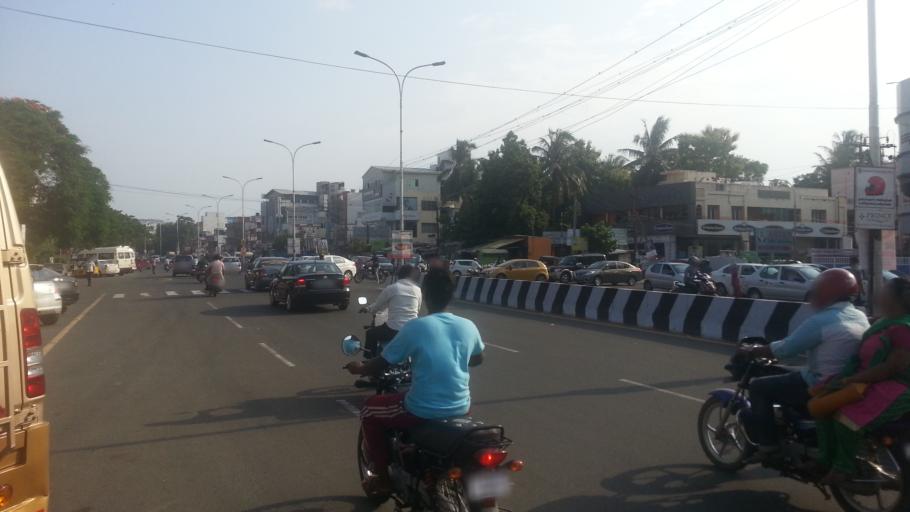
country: IN
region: Tamil Nadu
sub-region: Kancheepuram
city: Alandur
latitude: 12.9899
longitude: 80.2191
